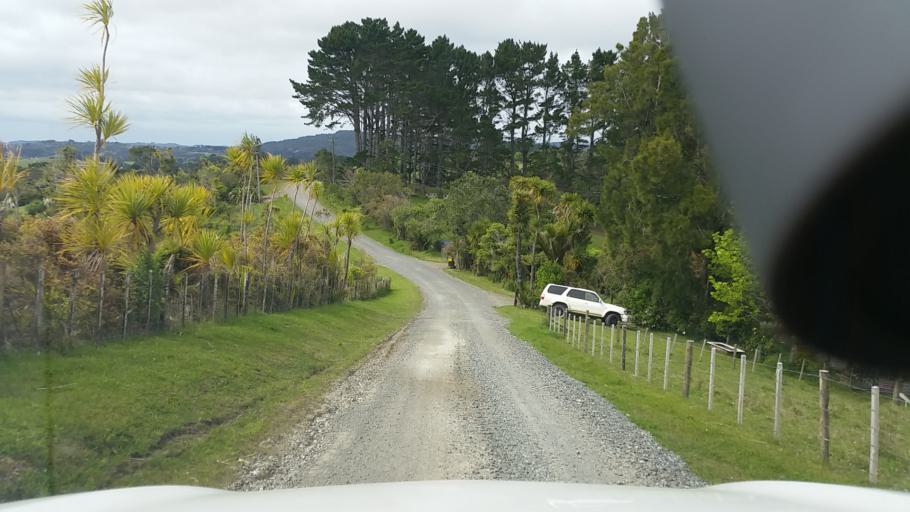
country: NZ
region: Auckland
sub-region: Auckland
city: Muriwai Beach
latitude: -36.8410
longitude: 174.5117
